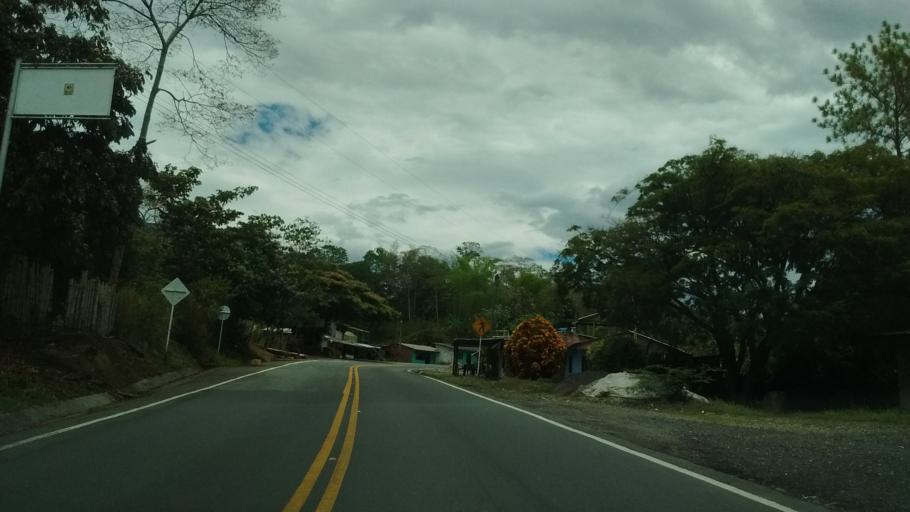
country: CO
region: Cauca
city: La Sierra
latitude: 2.2299
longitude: -76.7921
